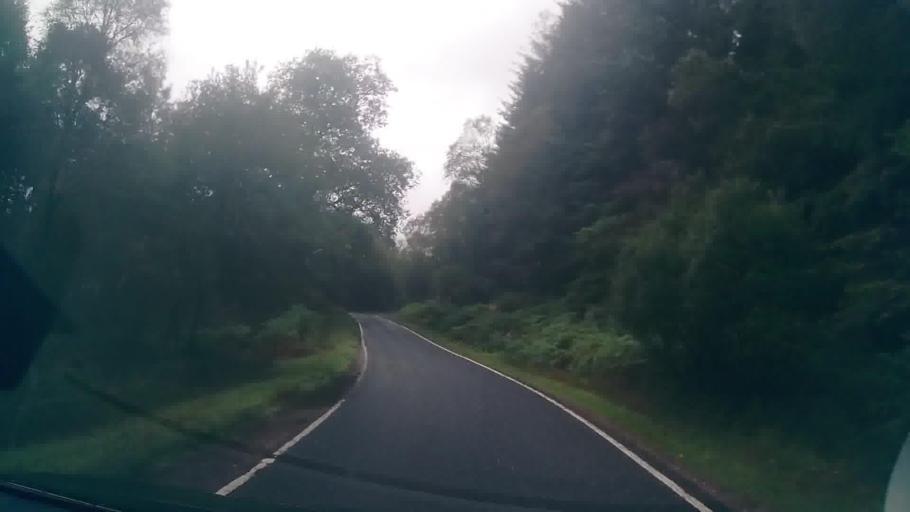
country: GB
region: Scotland
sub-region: Argyll and Bute
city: Isle Of Mull
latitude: 56.6866
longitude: -5.8090
